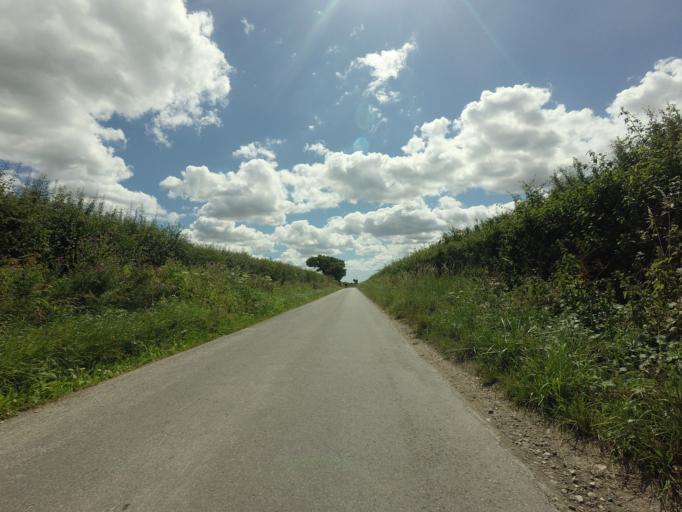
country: GB
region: England
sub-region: East Sussex
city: Seaford
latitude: 50.8574
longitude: 0.1525
